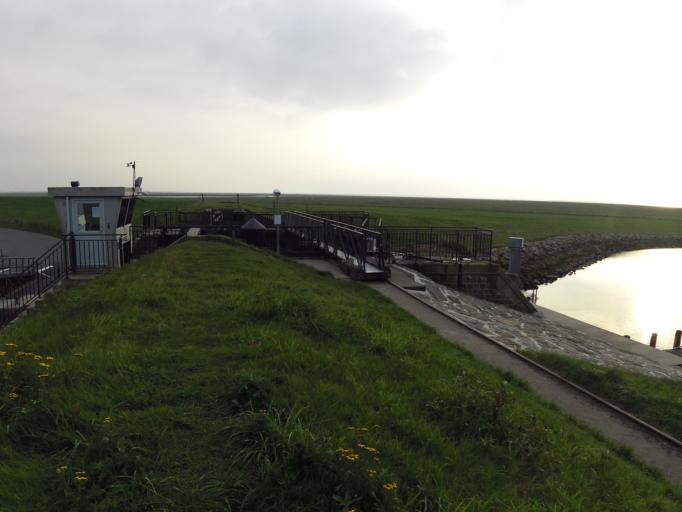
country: DK
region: South Denmark
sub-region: Esbjerg Kommune
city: Ribe
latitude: 55.3401
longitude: 8.6762
